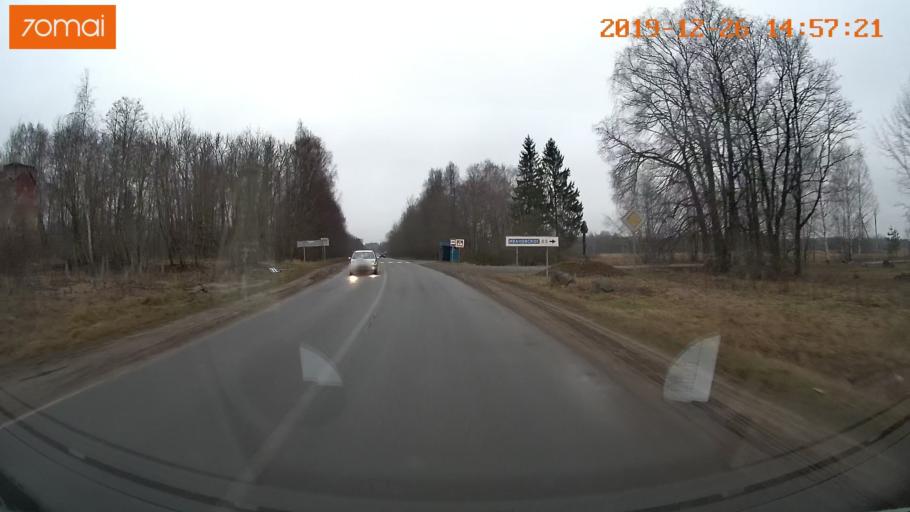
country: RU
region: Jaroslavl
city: Rybinsk
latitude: 58.2837
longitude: 38.8631
